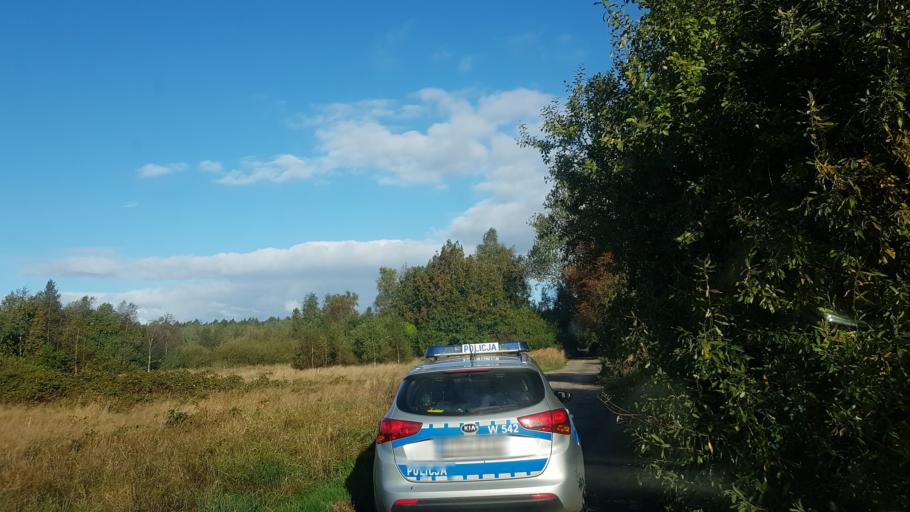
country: PL
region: West Pomeranian Voivodeship
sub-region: Powiat kolobrzeski
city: Grzybowo
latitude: 54.1668
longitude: 15.5160
